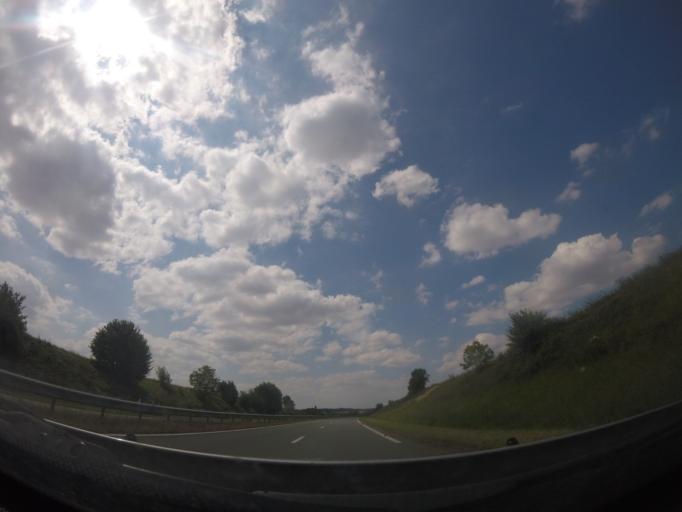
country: FR
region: Poitou-Charentes
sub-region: Departement de la Charente-Maritime
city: Saint-Porchaire
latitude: 45.8146
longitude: -0.7849
